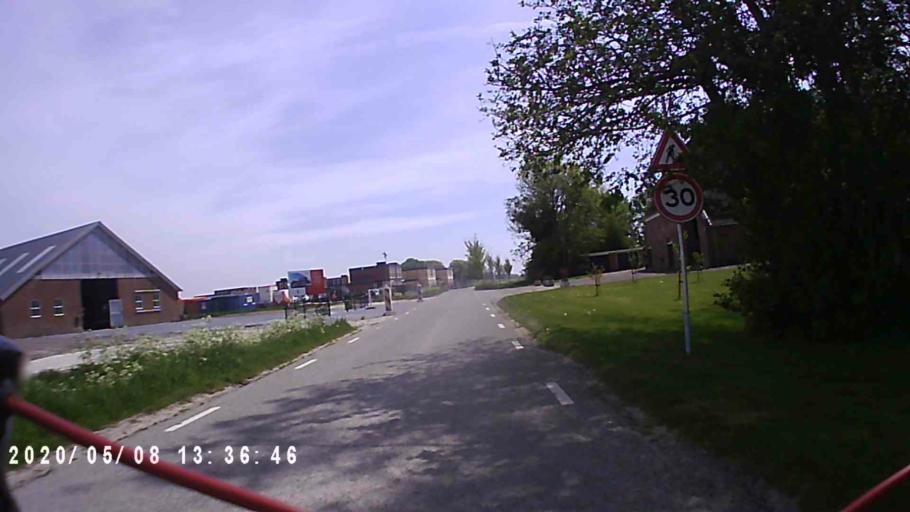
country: NL
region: Groningen
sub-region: Gemeente Appingedam
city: Appingedam
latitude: 53.3316
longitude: 6.7605
